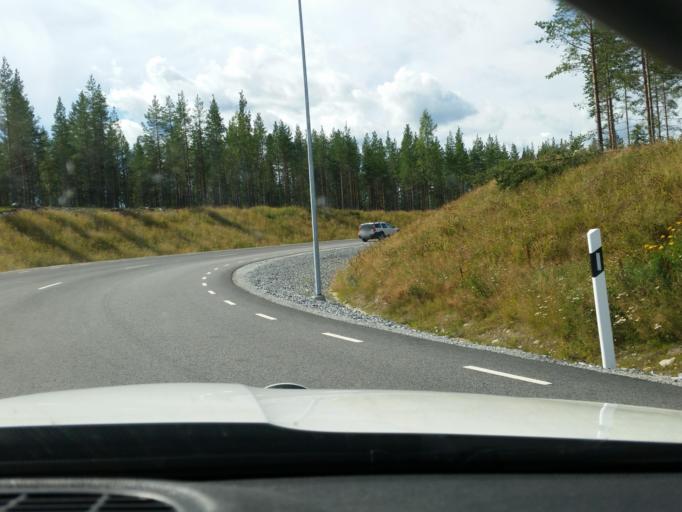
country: SE
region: Norrbotten
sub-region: Pitea Kommun
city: Norrfjarden
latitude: 65.3959
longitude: 21.4610
